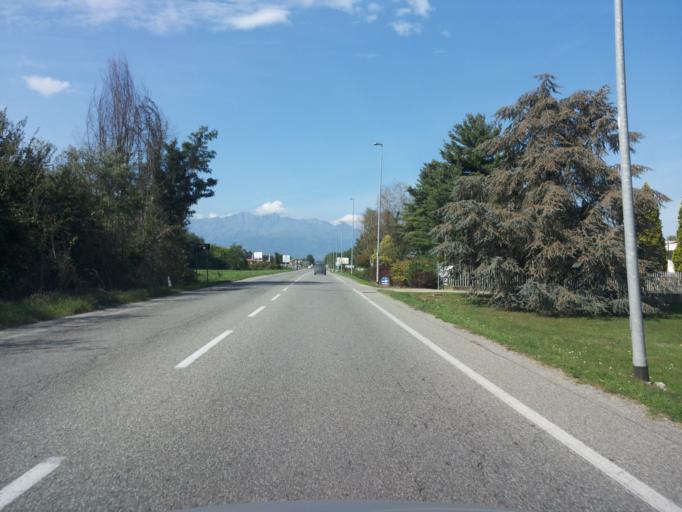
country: IT
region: Piedmont
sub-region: Provincia di Biella
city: Salussola
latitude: 45.4591
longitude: 8.1062
